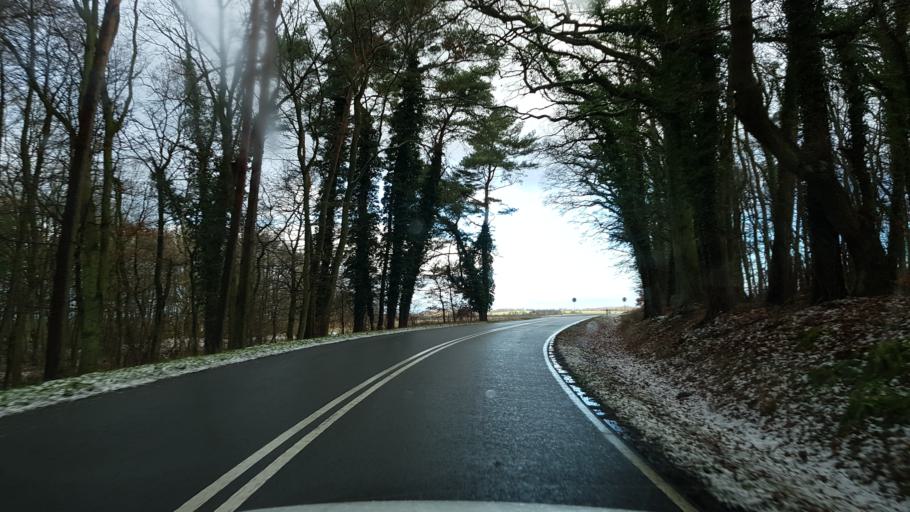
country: PL
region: West Pomeranian Voivodeship
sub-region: Powiat gryficki
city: Karnice
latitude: 54.0443
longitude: 15.0615
